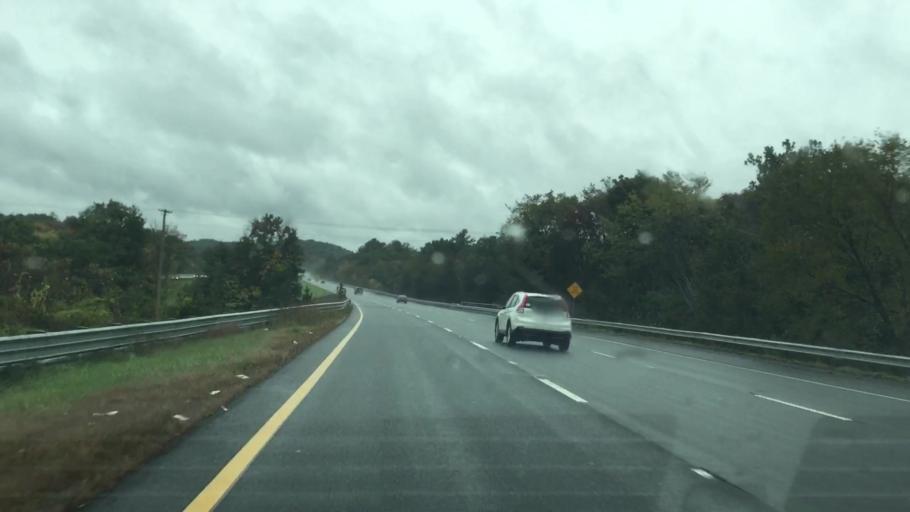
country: US
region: Massachusetts
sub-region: Essex County
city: Merrimac
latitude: 42.8179
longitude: -71.0214
